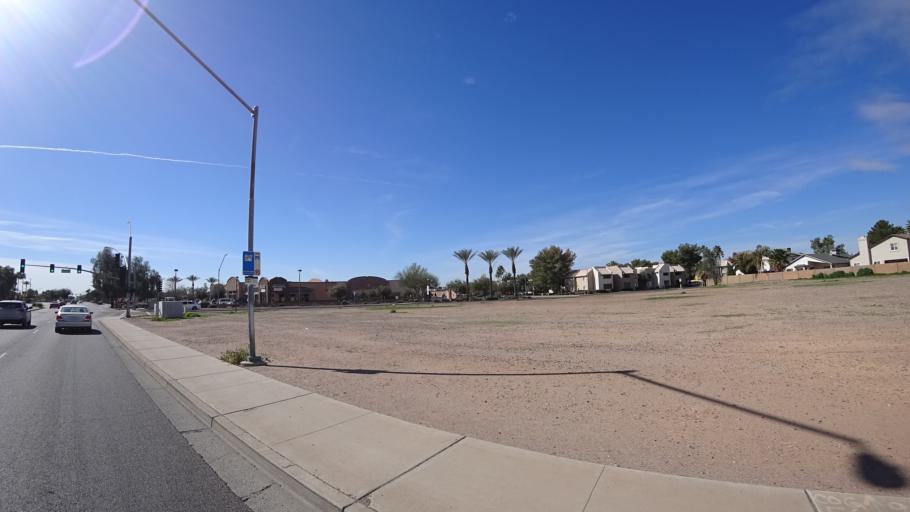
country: US
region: Arizona
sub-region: Maricopa County
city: Glendale
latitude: 33.5854
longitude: -112.1862
